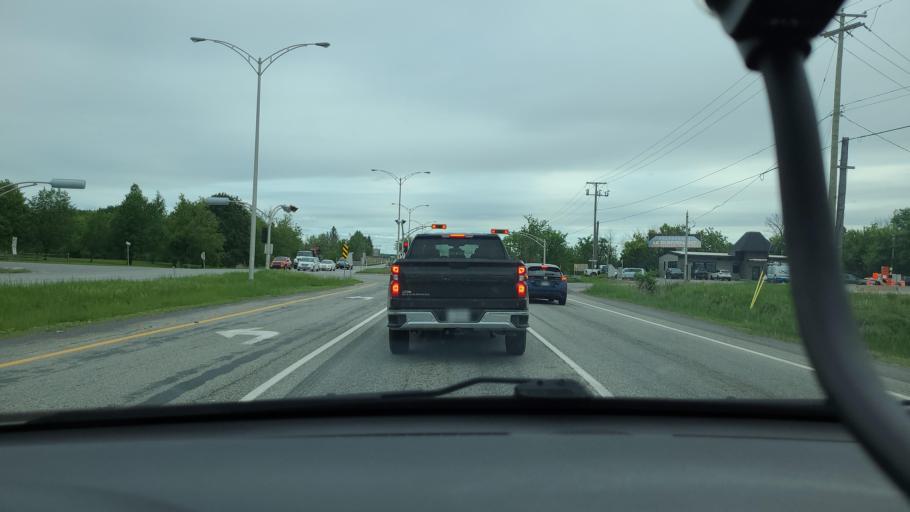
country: CA
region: Quebec
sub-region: Lanaudiere
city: Sainte-Julienne
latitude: 45.8965
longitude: -73.6597
